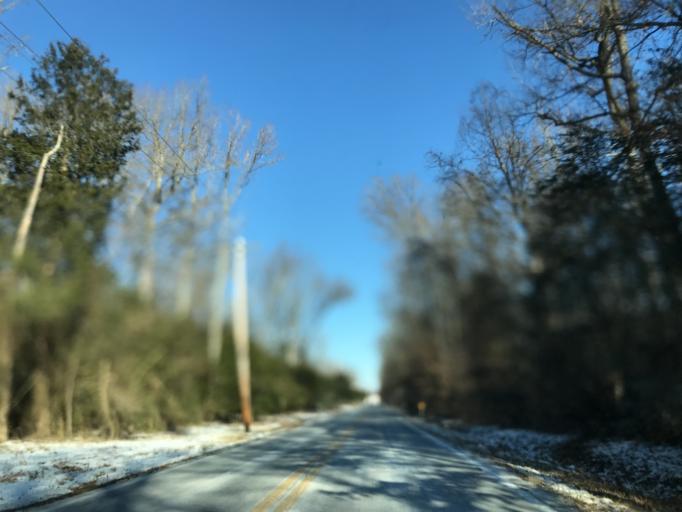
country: US
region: Maryland
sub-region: Charles County
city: La Plata
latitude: 38.4244
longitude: -76.9320
